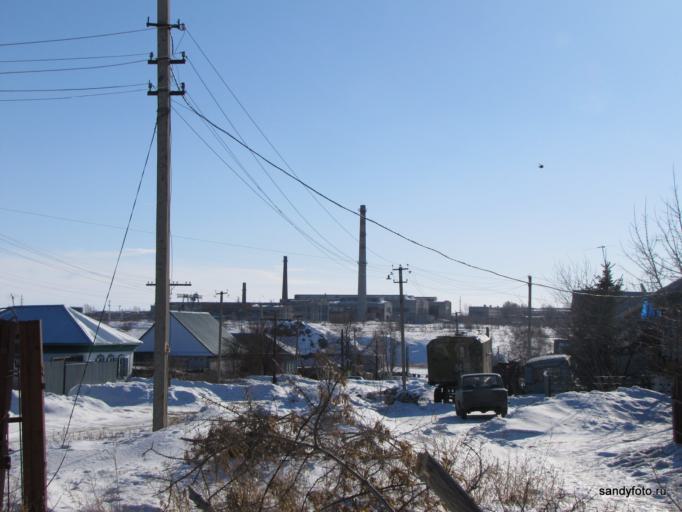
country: RU
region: Chelyabinsk
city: Troitsk
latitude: 54.0752
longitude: 61.5834
